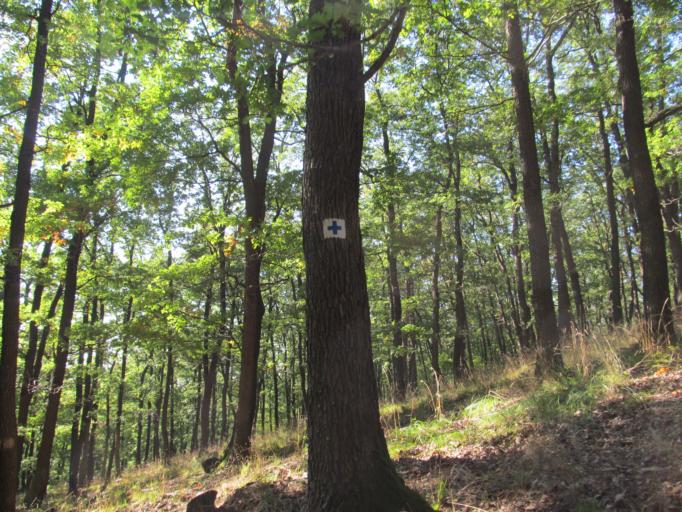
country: HU
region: Pest
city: Szob
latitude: 47.8967
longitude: 18.8195
